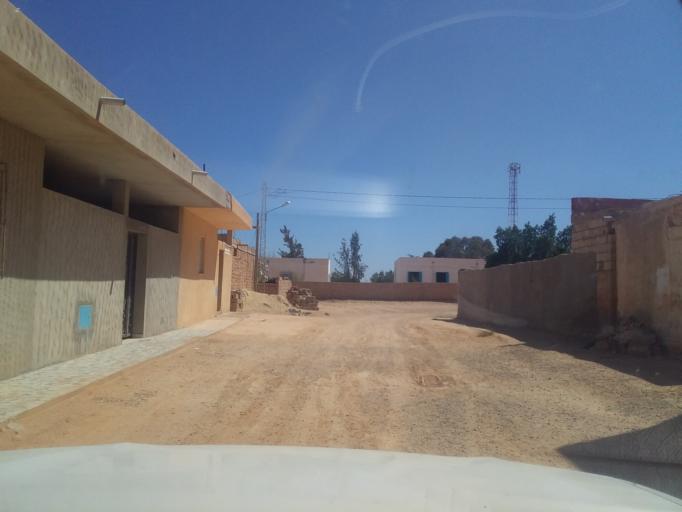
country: TN
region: Qabis
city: Matmata
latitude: 33.5151
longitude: 10.2189
